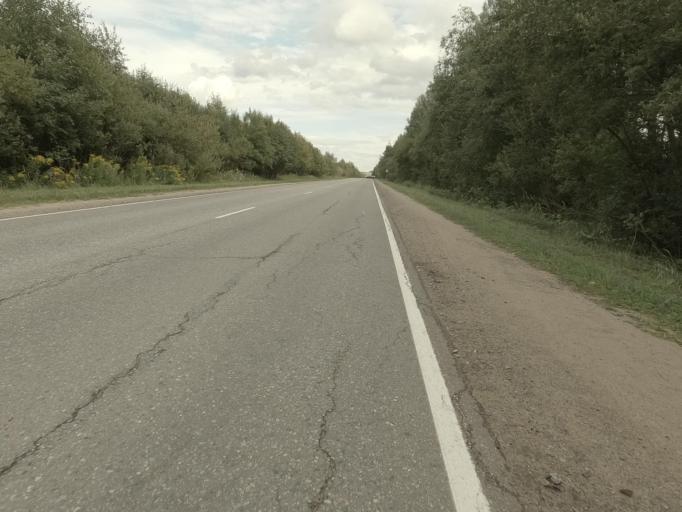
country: RU
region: Leningrad
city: Mga
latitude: 59.7616
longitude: 31.0005
